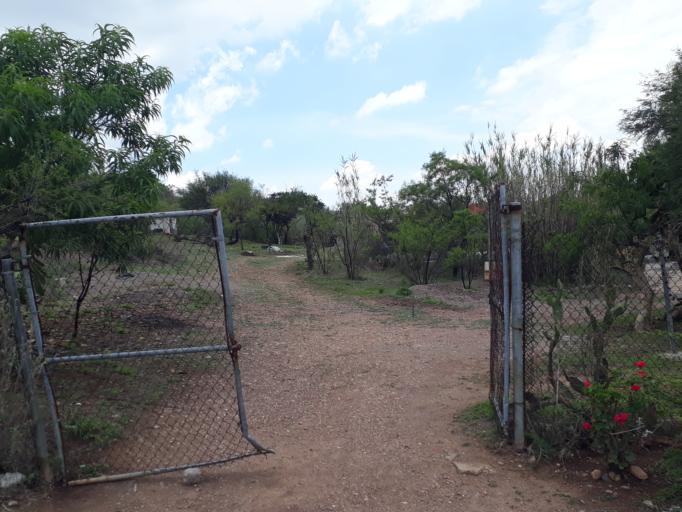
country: MX
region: Aguascalientes
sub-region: Aguascalientes
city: San Sebastian [Fraccionamiento]
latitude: 21.7869
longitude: -102.2479
